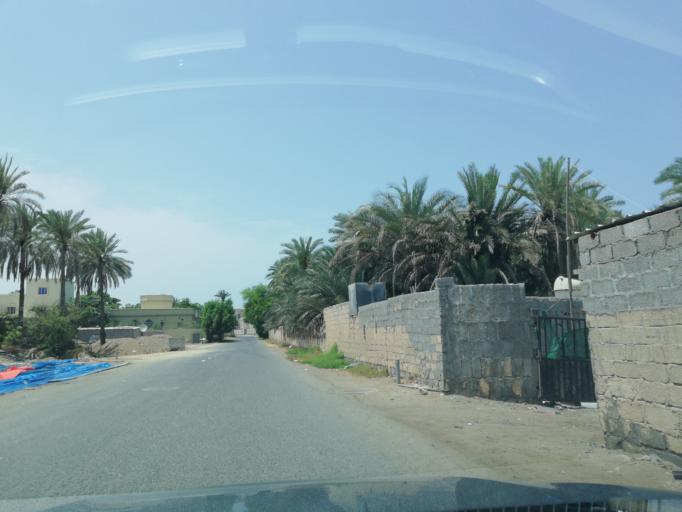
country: OM
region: Muhafazat Masqat
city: As Sib al Jadidah
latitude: 23.6582
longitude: 58.2129
